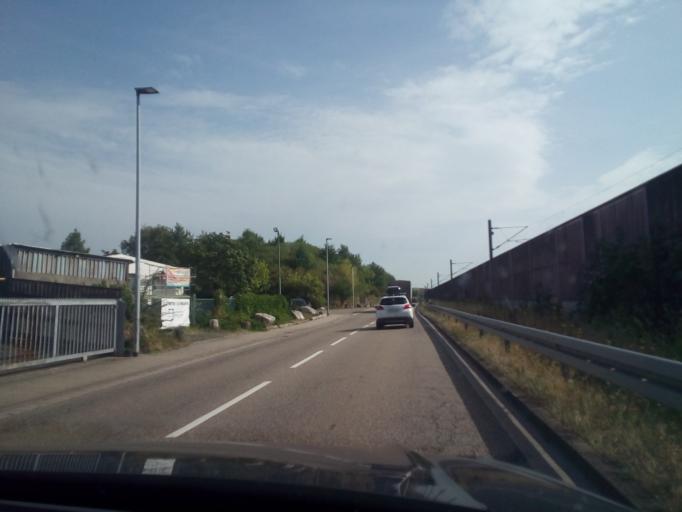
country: DE
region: Baden-Wuerttemberg
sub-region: Karlsruhe Region
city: Sinzheim
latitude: 48.7737
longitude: 8.1724
